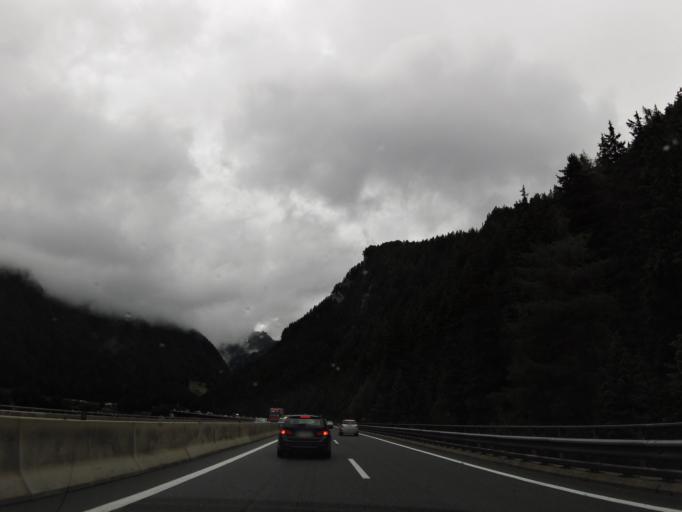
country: AT
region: Tyrol
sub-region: Politischer Bezirk Innsbruck Land
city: Gries am Brenner
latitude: 47.0290
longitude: 11.4888
